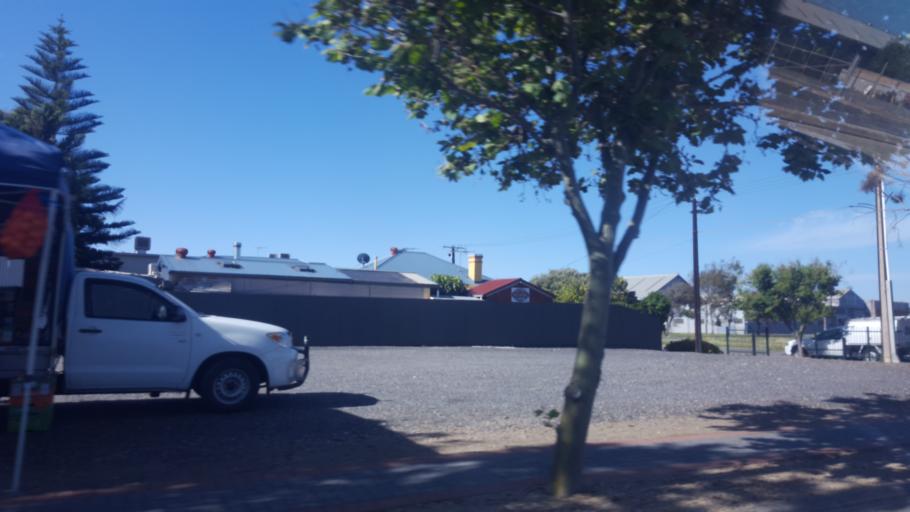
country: AU
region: South Australia
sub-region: Port Adelaide Enfield
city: Alberton
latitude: -34.8523
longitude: 138.5062
